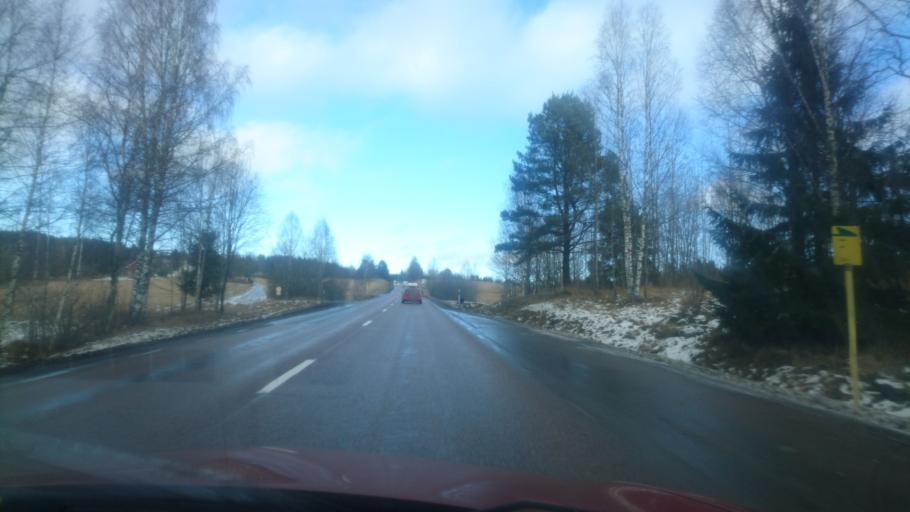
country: SE
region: Vaermland
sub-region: Sunne Kommun
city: Sunne
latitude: 59.6938
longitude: 13.1431
